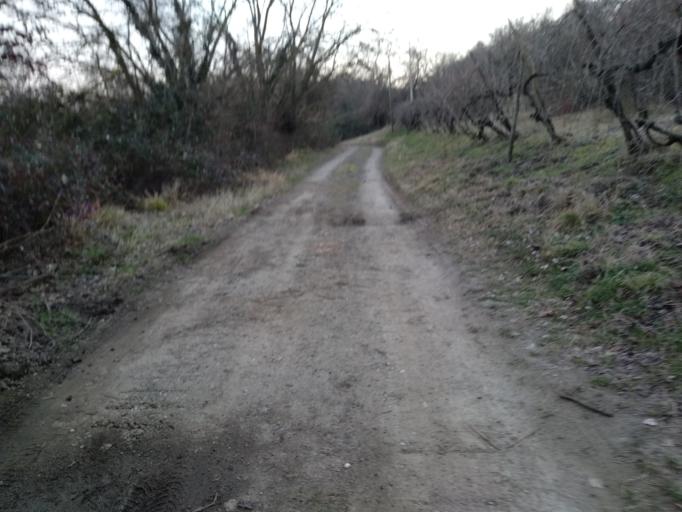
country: IT
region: Veneto
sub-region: Provincia di Padova
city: Battaglia Terme
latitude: 45.3004
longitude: 11.7744
